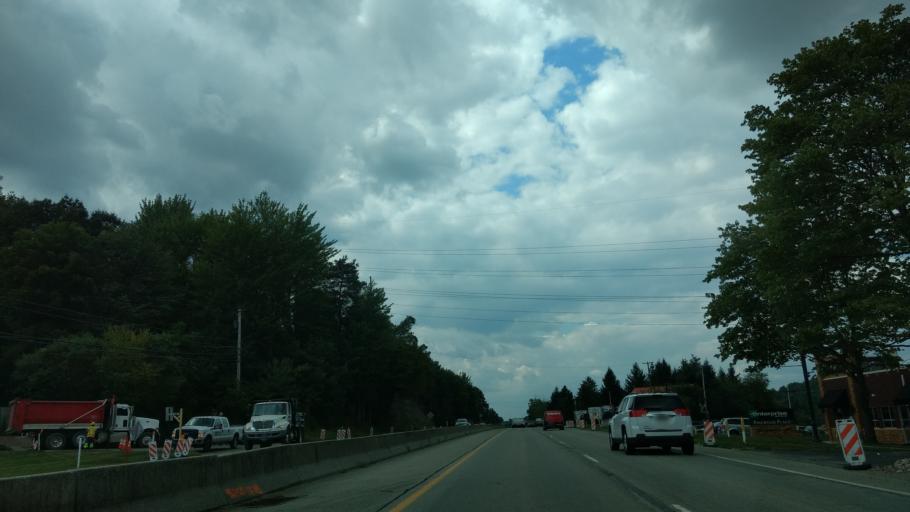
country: US
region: Pennsylvania
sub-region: Allegheny County
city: Bradford Woods
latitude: 40.6514
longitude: -80.0808
